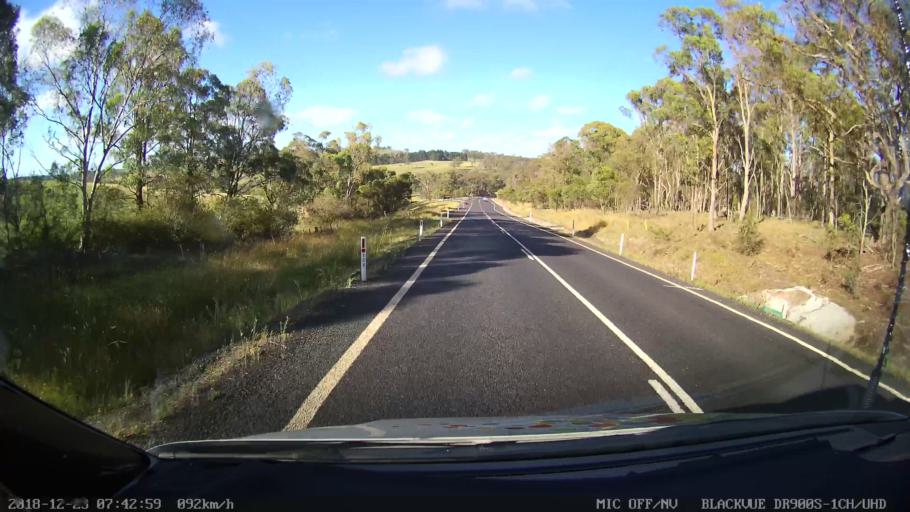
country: AU
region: New South Wales
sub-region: Armidale Dumaresq
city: Enmore
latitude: -30.5187
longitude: 151.9709
